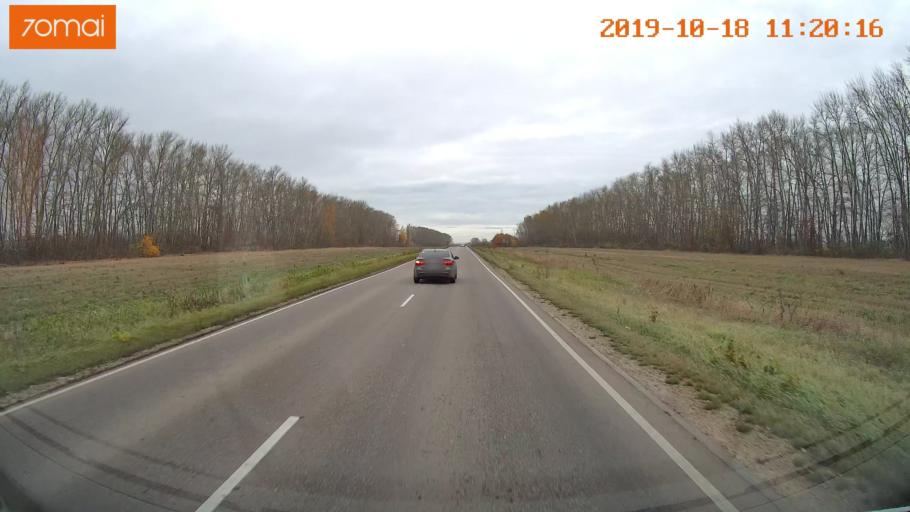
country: RU
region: Tula
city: Kimovsk
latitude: 54.0579
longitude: 38.5577
